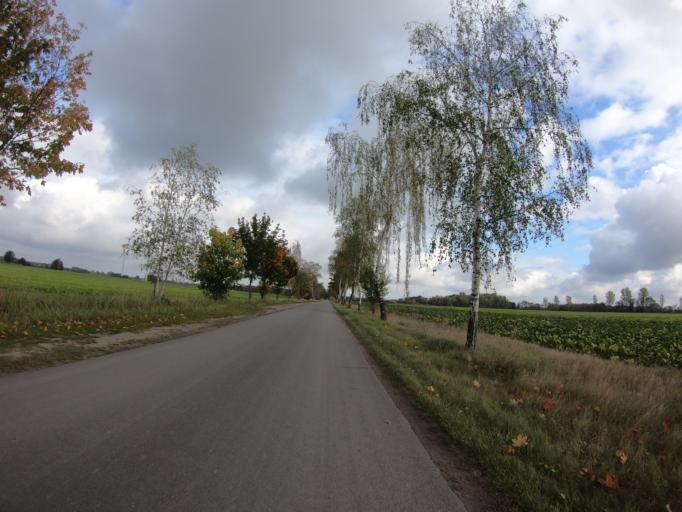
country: DE
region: Lower Saxony
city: Wahrenholz
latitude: 52.5919
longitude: 10.5813
